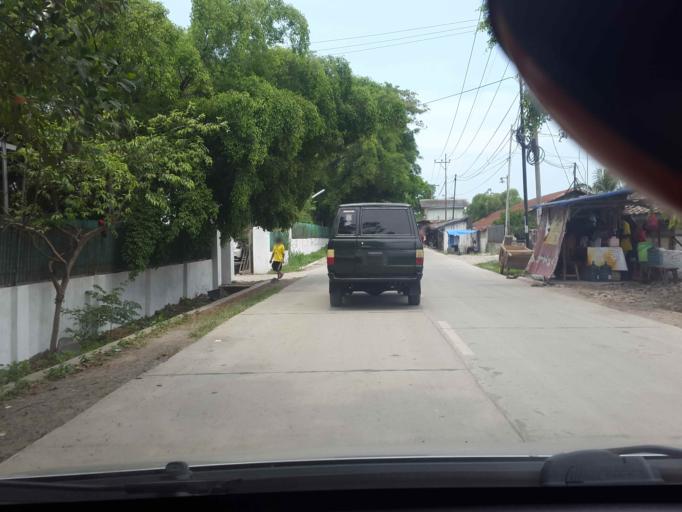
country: ID
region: Lampung
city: Panjang
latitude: -5.4443
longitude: 105.3016
